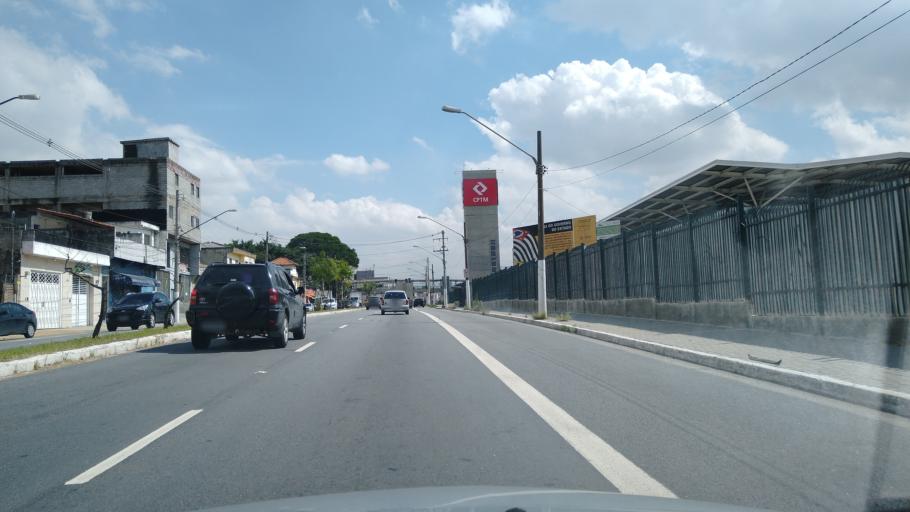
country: BR
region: Sao Paulo
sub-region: Guarulhos
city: Guarulhos
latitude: -23.4978
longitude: -46.5182
